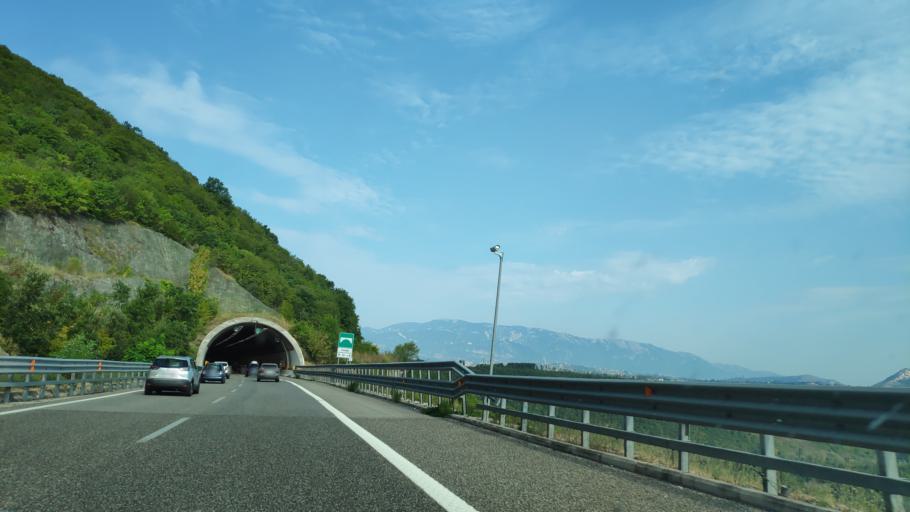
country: IT
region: Campania
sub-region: Provincia di Salerno
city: Sicignano degli Alburni
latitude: 40.6000
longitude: 15.3113
